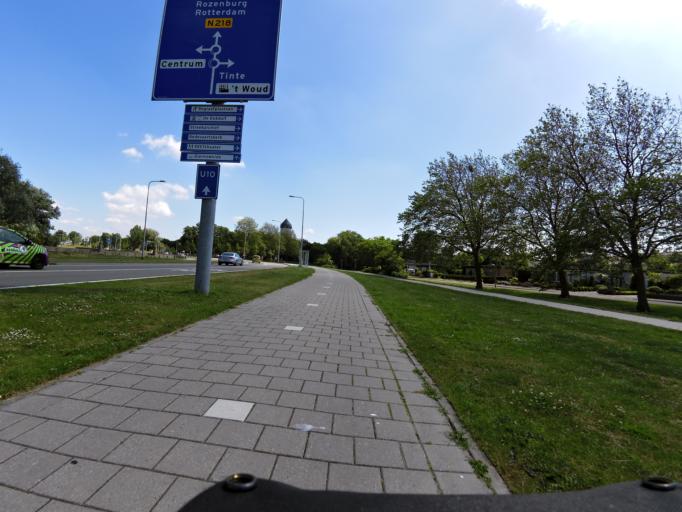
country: NL
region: South Holland
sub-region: Gemeente Brielle
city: Brielle
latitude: 51.9002
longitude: 4.1576
